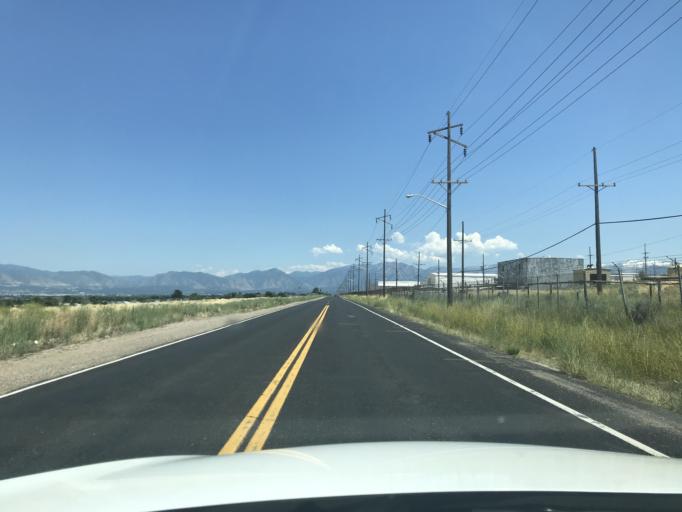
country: US
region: Utah
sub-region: Salt Lake County
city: Magna
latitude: 40.6820
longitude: -112.0710
